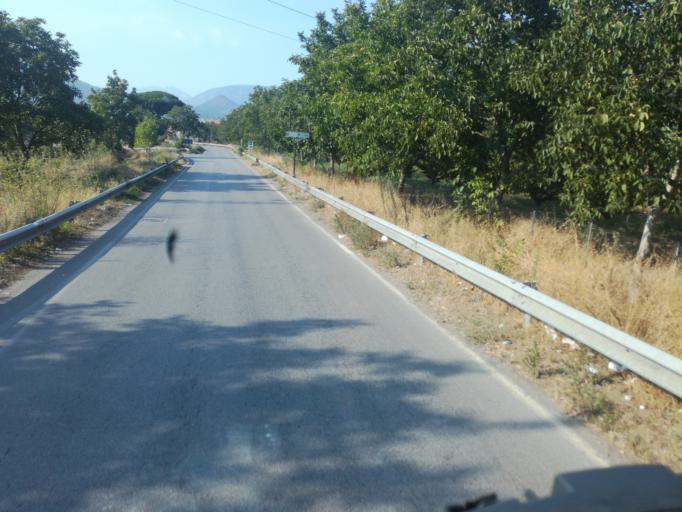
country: IT
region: Campania
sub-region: Provincia di Salerno
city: Piazza di Pandola
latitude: 40.7980
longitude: 14.7712
